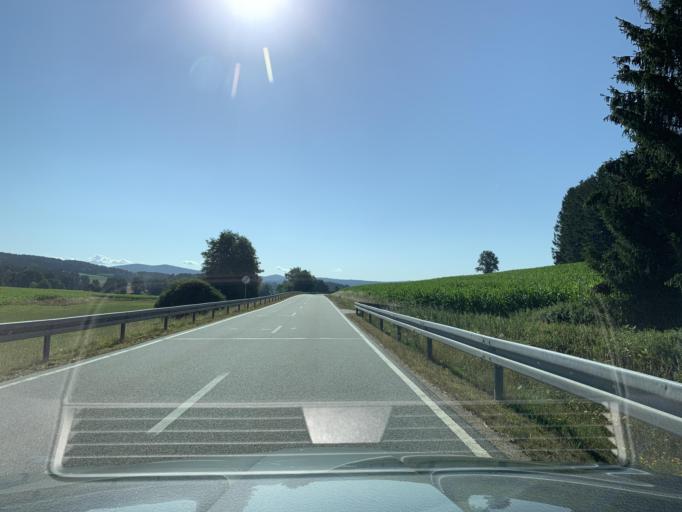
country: DE
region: Bavaria
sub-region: Upper Palatinate
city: Pettendorf
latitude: 49.3601
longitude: 12.3494
